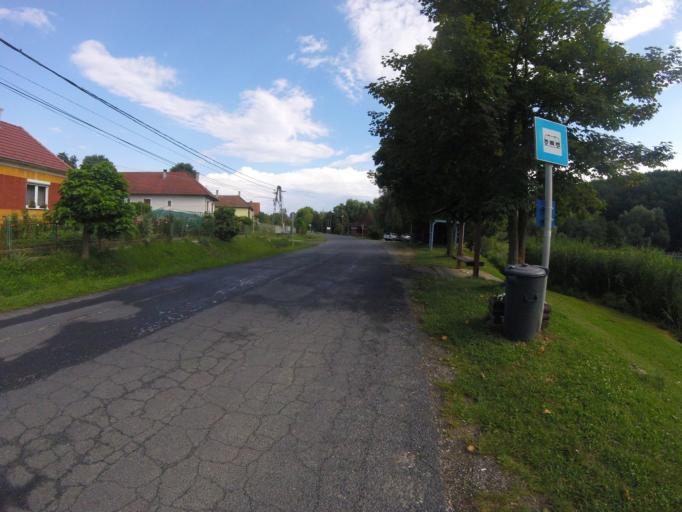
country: HU
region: Zala
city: Becsehely
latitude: 46.4927
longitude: 16.7434
